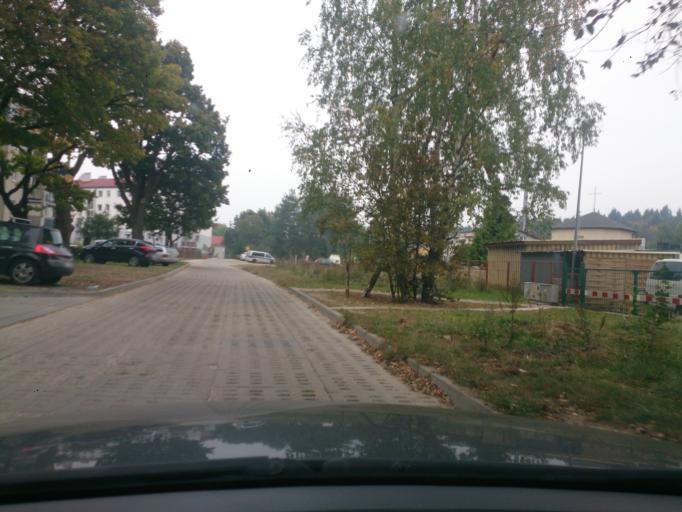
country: PL
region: Pomeranian Voivodeship
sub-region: Gdynia
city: Wielki Kack
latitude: 54.4675
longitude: 18.4817
